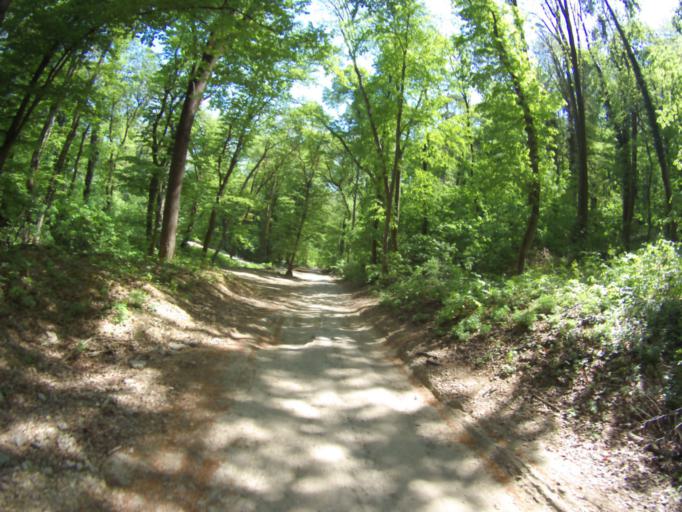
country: HU
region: Pest
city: Budaors
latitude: 47.4839
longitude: 18.9677
